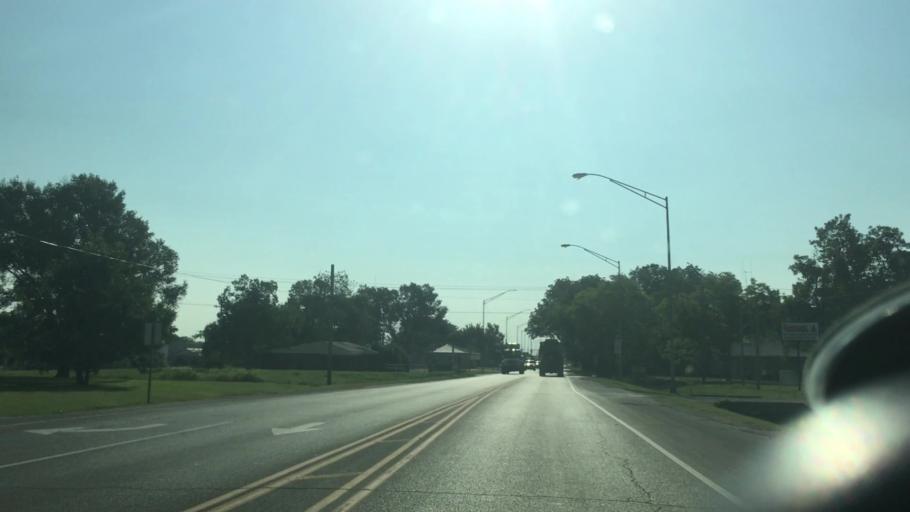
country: US
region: Oklahoma
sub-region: Garvin County
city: Lindsay
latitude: 34.8370
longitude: -97.6150
